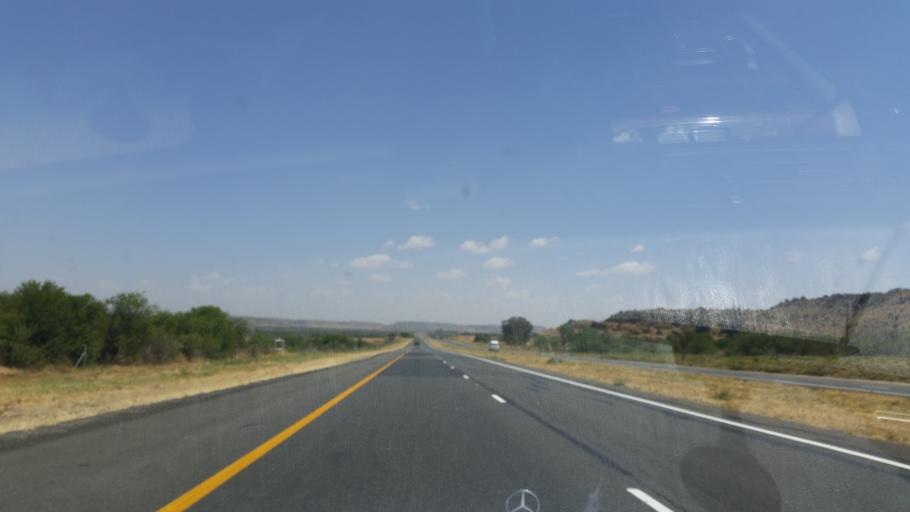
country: ZA
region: Orange Free State
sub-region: Mangaung Metropolitan Municipality
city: Bloemfontein
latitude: -28.9539
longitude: 26.3890
